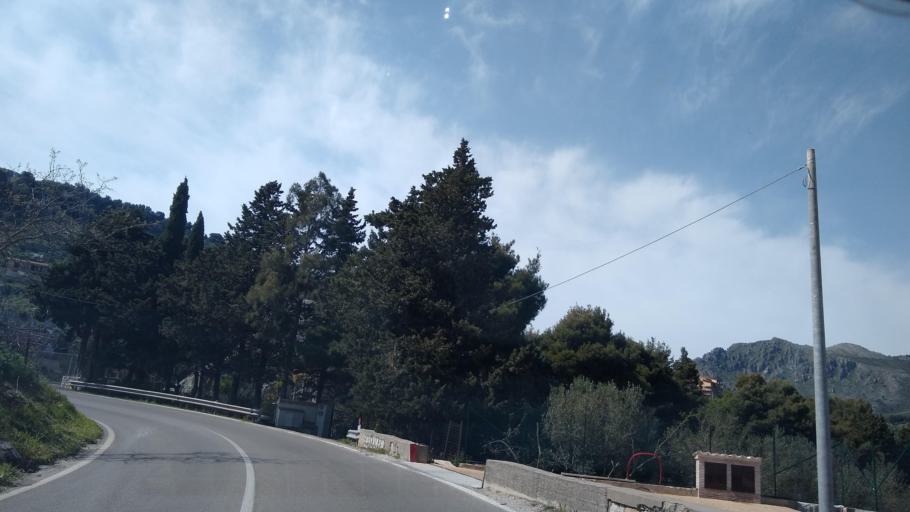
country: IT
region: Sicily
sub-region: Palermo
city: Giacalone
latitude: 38.0373
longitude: 13.2172
